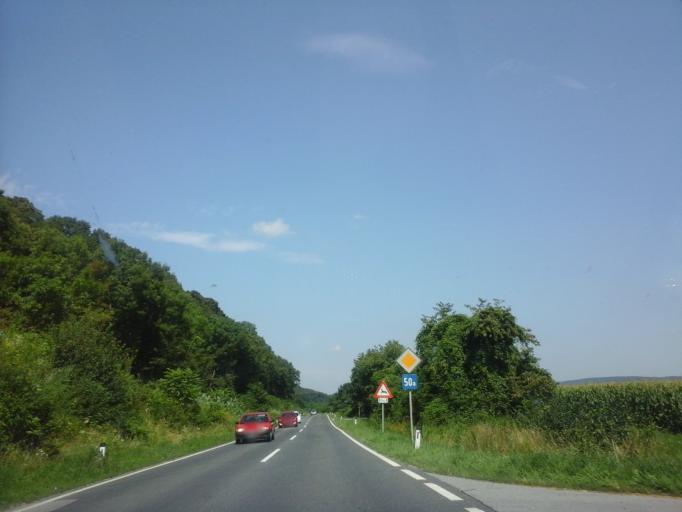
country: AT
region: Lower Austria
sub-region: Politischer Bezirk Bruck an der Leitha
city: Berg
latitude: 48.1073
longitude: 17.0427
